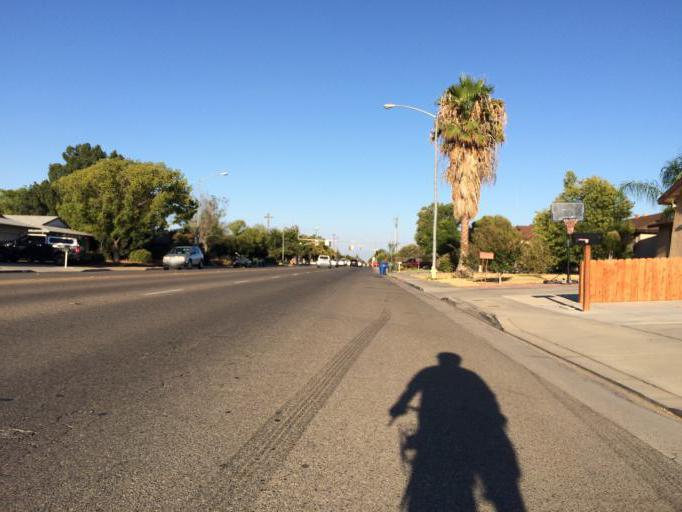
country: US
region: California
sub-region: Fresno County
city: Clovis
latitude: 36.8157
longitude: -119.6840
